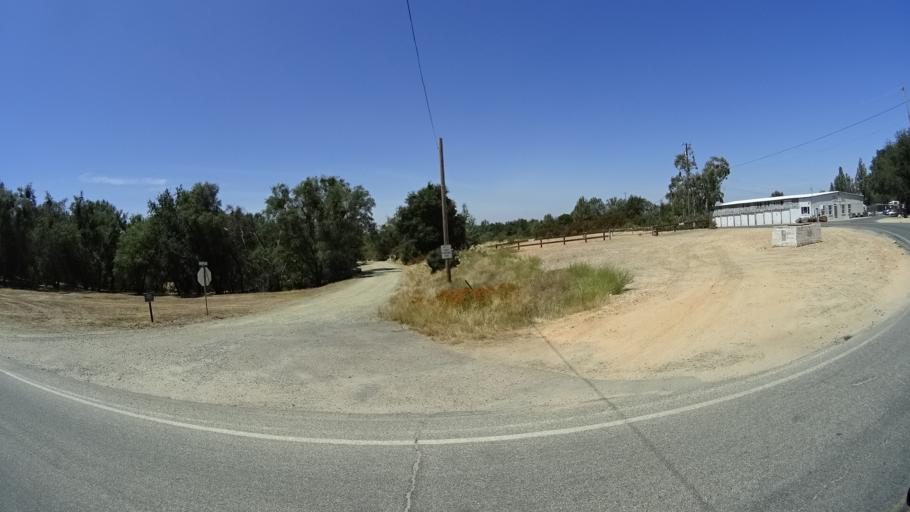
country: US
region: California
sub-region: Calaveras County
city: Valley Springs
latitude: 38.2123
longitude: -120.9077
